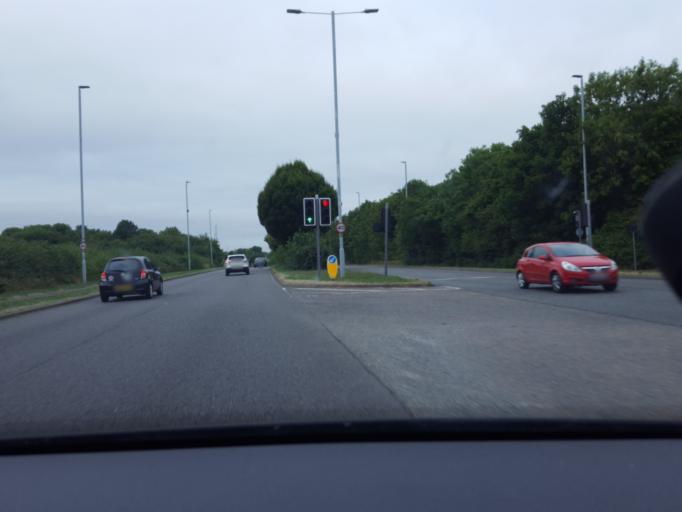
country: GB
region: England
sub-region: Leicestershire
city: Hathern
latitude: 52.7617
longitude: -1.2539
